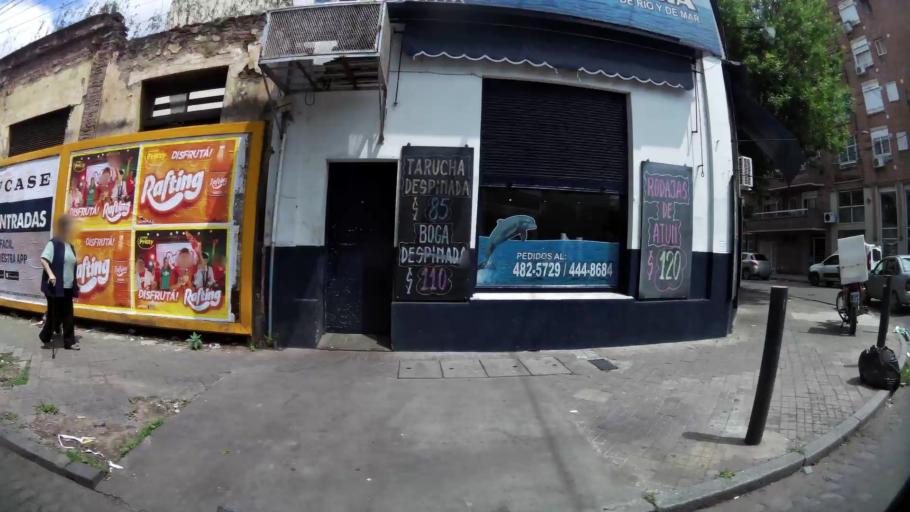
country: AR
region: Santa Fe
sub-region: Departamento de Rosario
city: Rosario
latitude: -32.9611
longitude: -60.6403
